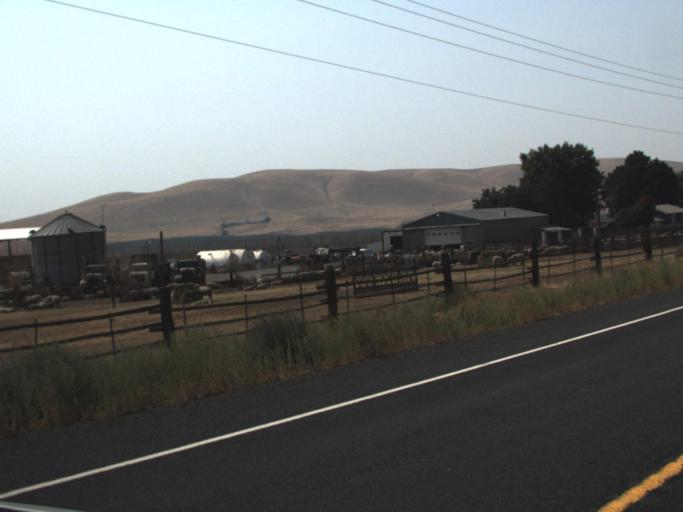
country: US
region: Washington
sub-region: Yakima County
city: Zillah
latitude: 46.5202
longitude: -120.2186
